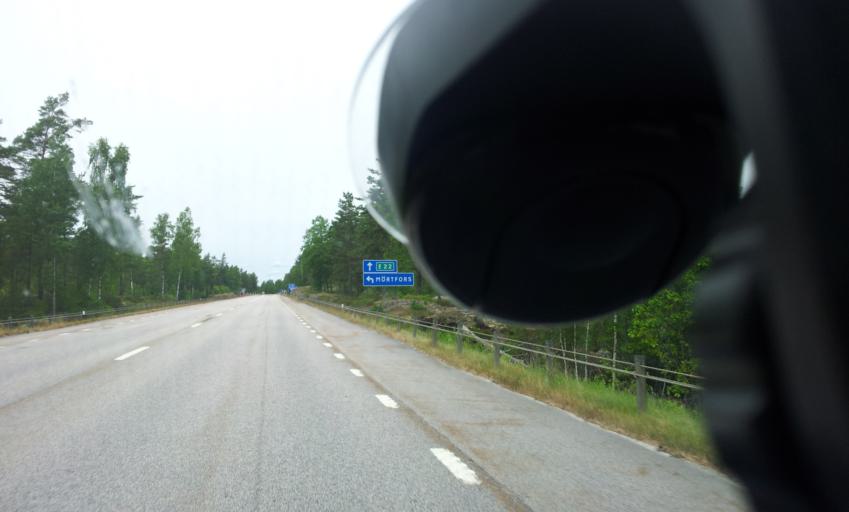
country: SE
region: Kalmar
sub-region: Vasterviks Kommun
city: Ankarsrum
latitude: 57.5207
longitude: 16.4959
